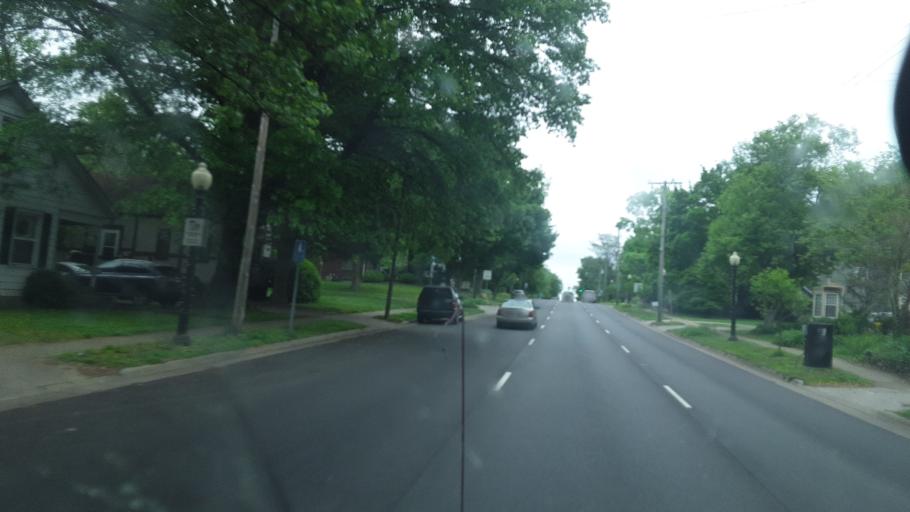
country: US
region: Illinois
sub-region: Jackson County
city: Carbondale
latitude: 37.7246
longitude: -89.2245
